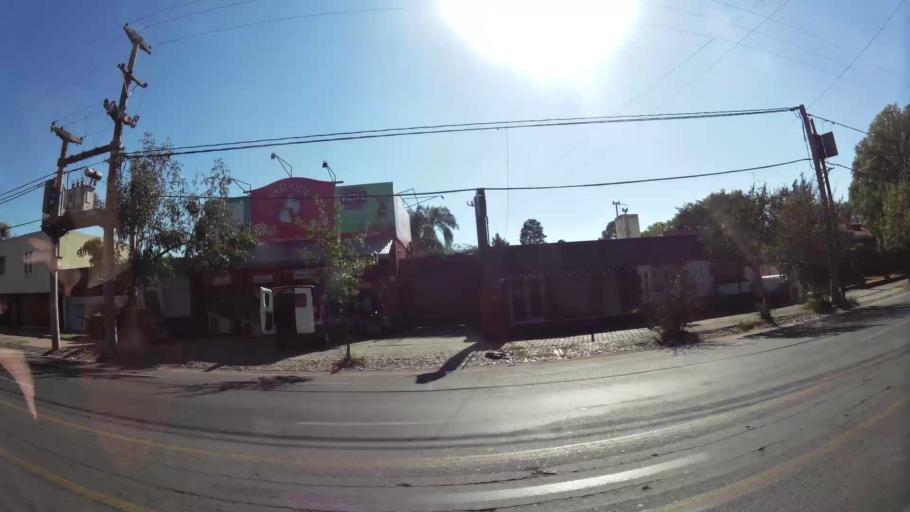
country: AR
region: Cordoba
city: Villa Allende
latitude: -31.3547
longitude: -64.2460
